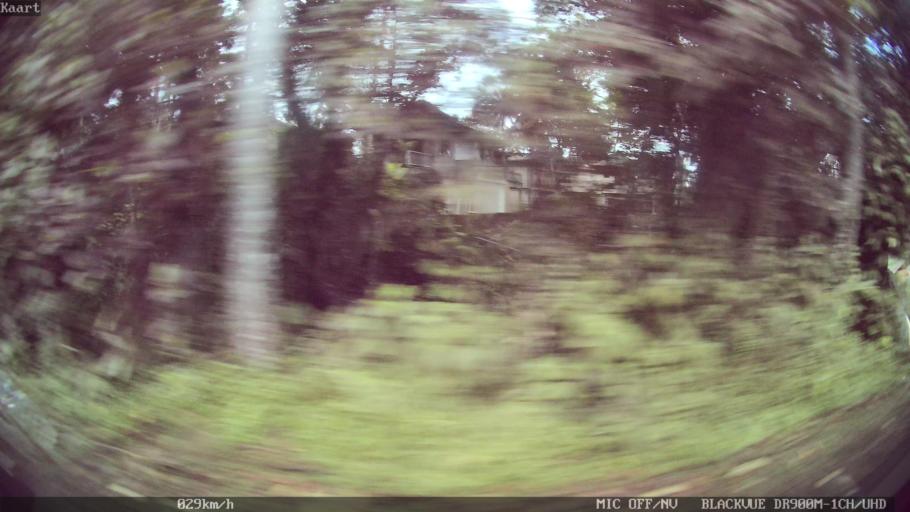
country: ID
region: Bali
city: Banjar Pesalakan
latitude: -8.4849
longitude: 115.2974
